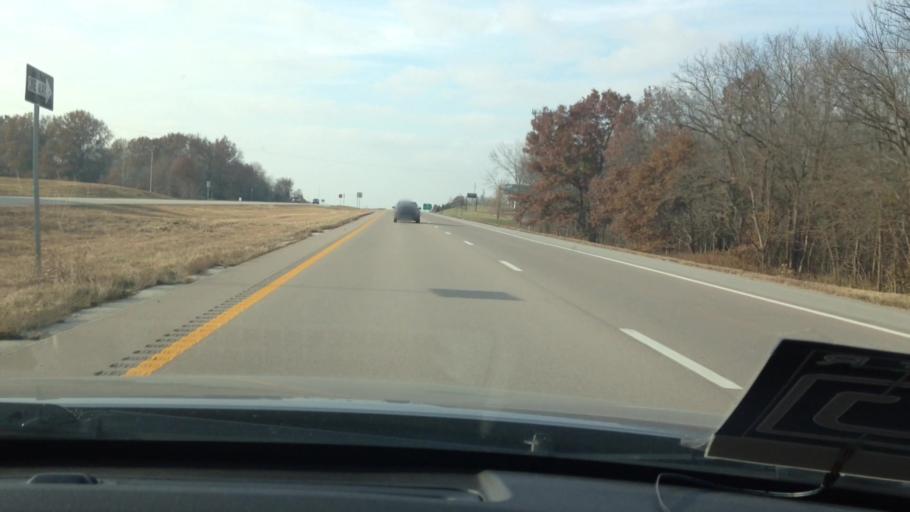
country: US
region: Missouri
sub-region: Cass County
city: Garden City
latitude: 38.4963
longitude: -94.0621
